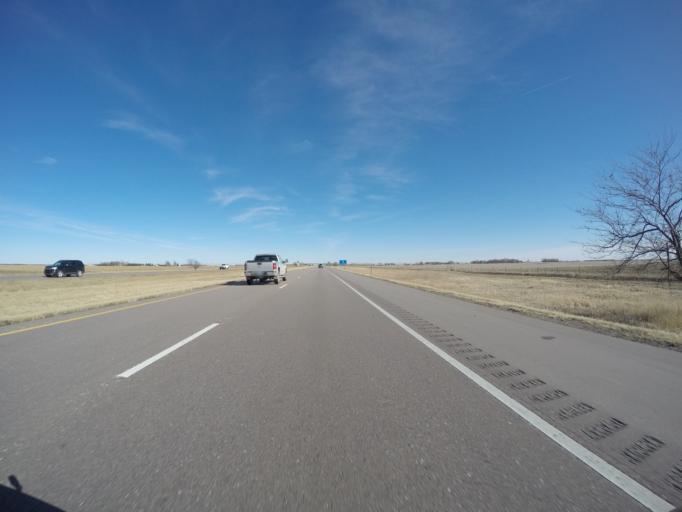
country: US
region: Nebraska
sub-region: York County
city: York
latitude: 40.8212
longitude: -97.6268
